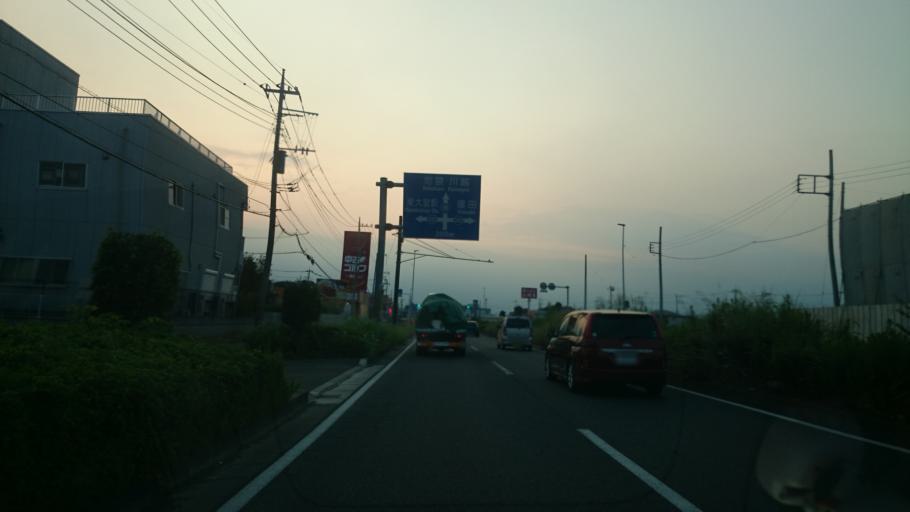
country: JP
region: Saitama
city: Hasuda
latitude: 35.9573
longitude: 139.6578
